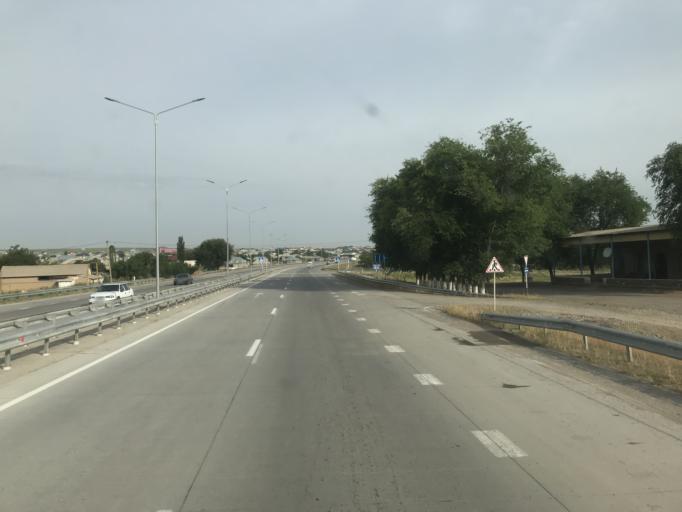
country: KZ
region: Ongtustik Qazaqstan
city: Qazyqurt
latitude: 41.7840
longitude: 69.3988
